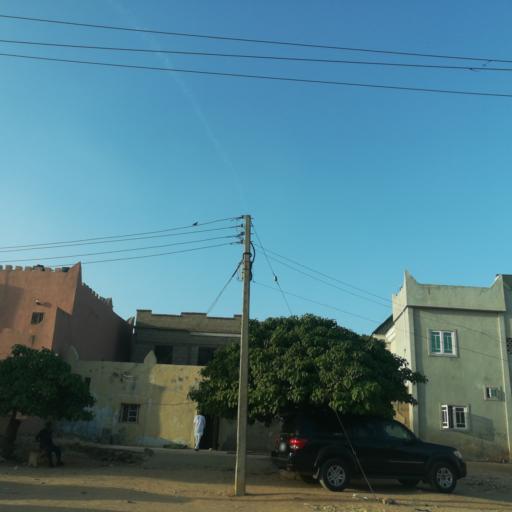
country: NG
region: Kano
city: Kano
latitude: 11.9907
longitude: 8.5278
